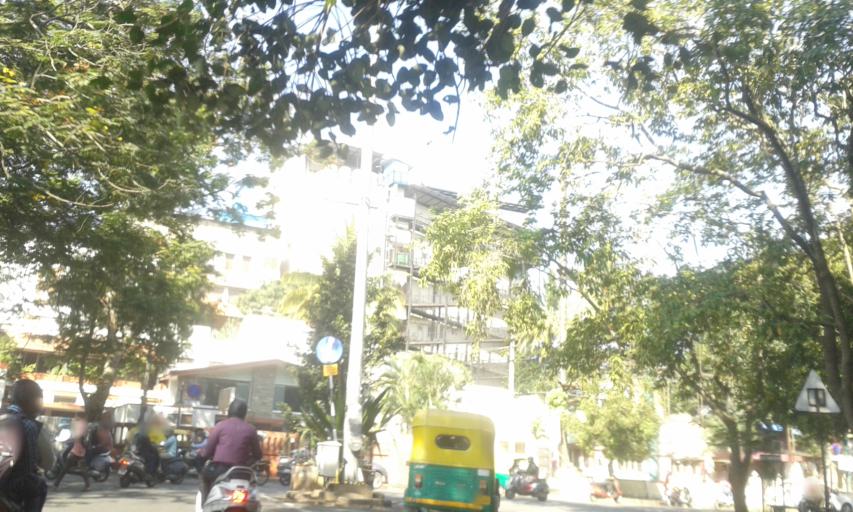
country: IN
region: Karnataka
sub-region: Bangalore Urban
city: Bangalore
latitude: 12.9360
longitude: 77.5852
